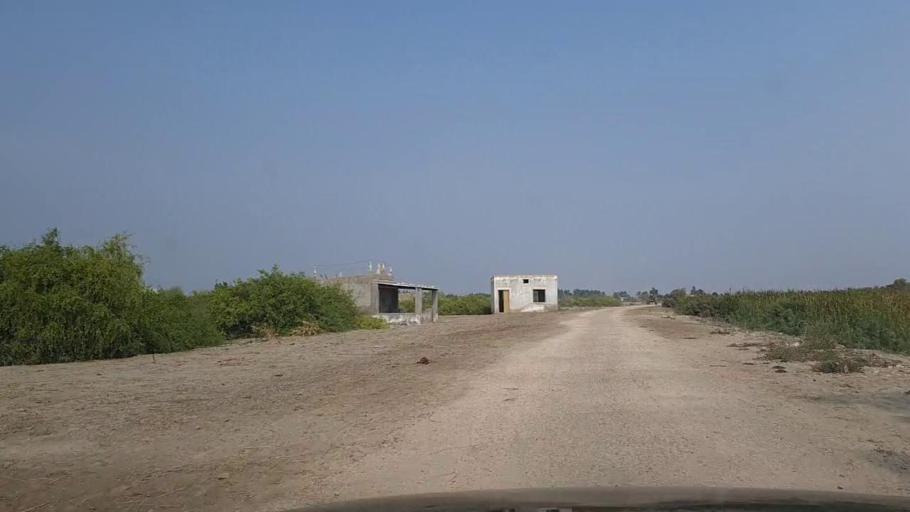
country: PK
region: Sindh
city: Thatta
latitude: 24.7489
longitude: 67.7977
